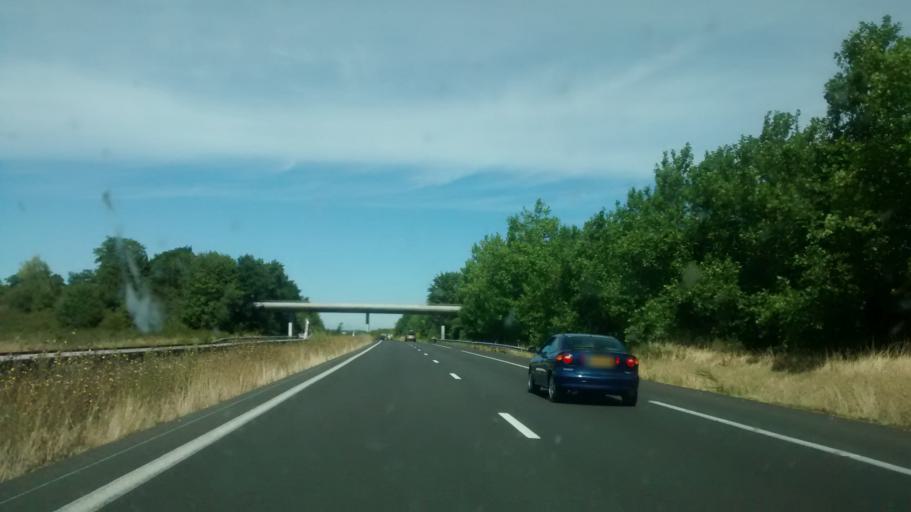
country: FR
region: Poitou-Charentes
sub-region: Departement de la Charente-Maritime
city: Thenac
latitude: 45.6703
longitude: -0.6383
